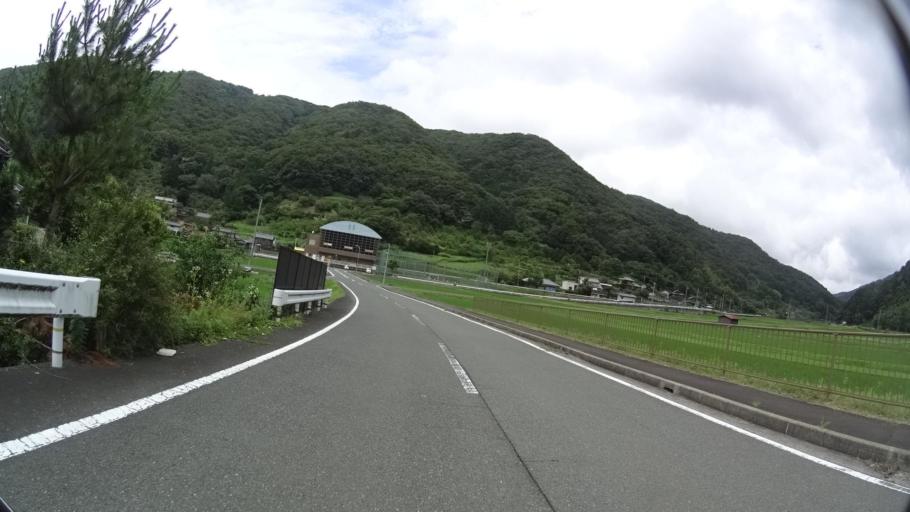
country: JP
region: Kyoto
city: Maizuru
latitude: 35.5224
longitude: 135.3452
